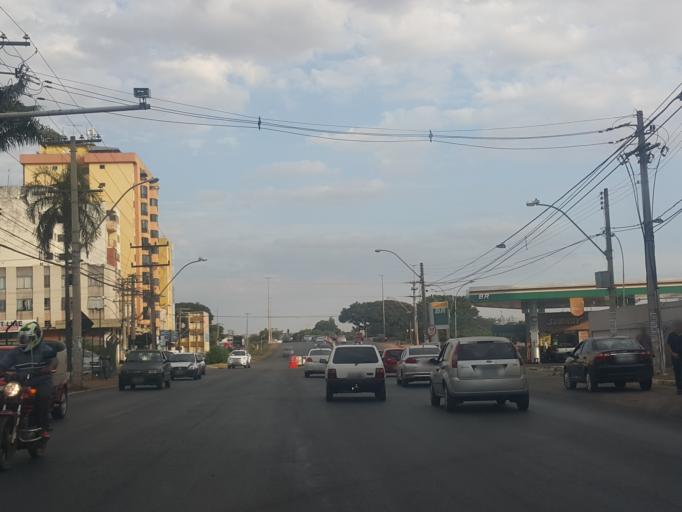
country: BR
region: Federal District
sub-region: Brasilia
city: Brasilia
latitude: -15.8327
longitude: -48.0610
